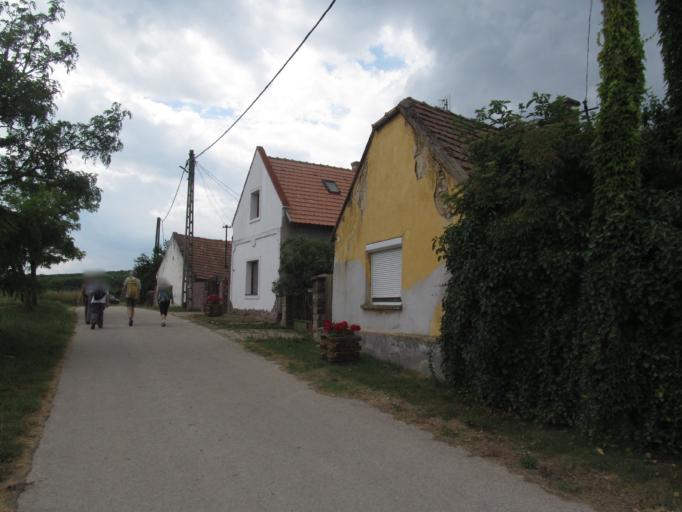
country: HU
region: Veszprem
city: Badacsonytomaj
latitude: 46.8471
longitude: 17.5564
